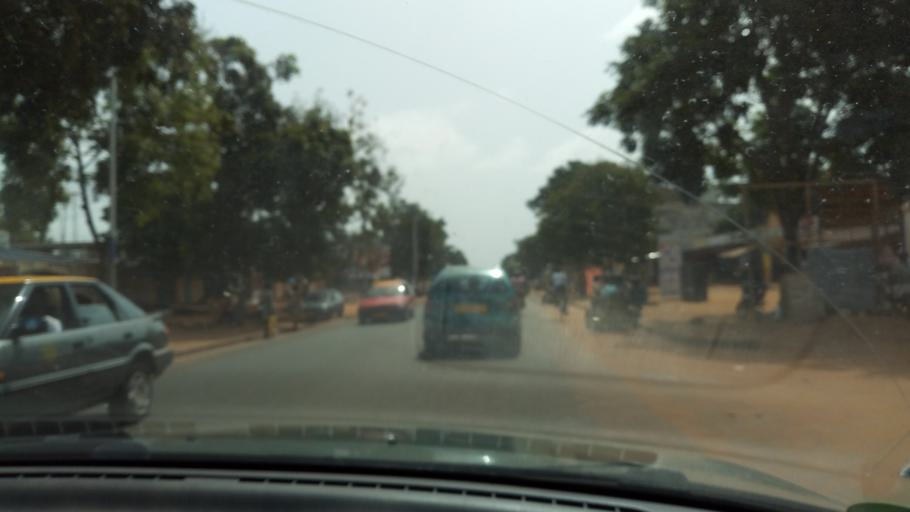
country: TG
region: Maritime
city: Lome
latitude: 6.1769
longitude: 1.1786
